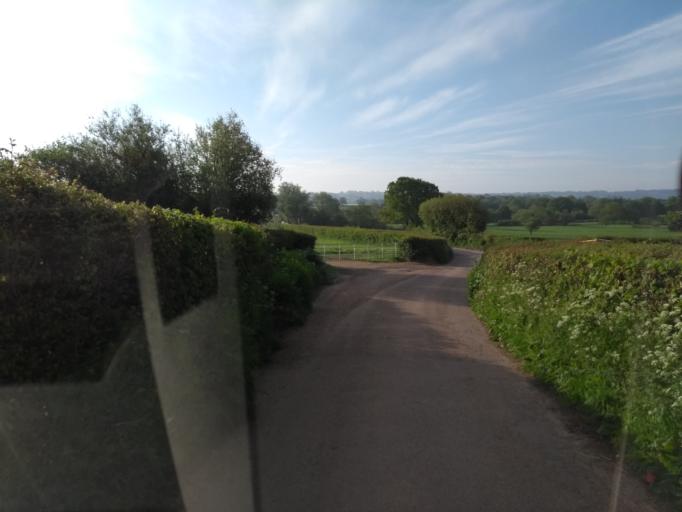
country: GB
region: England
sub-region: Devon
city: Axminster
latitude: 50.8195
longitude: -2.9610
